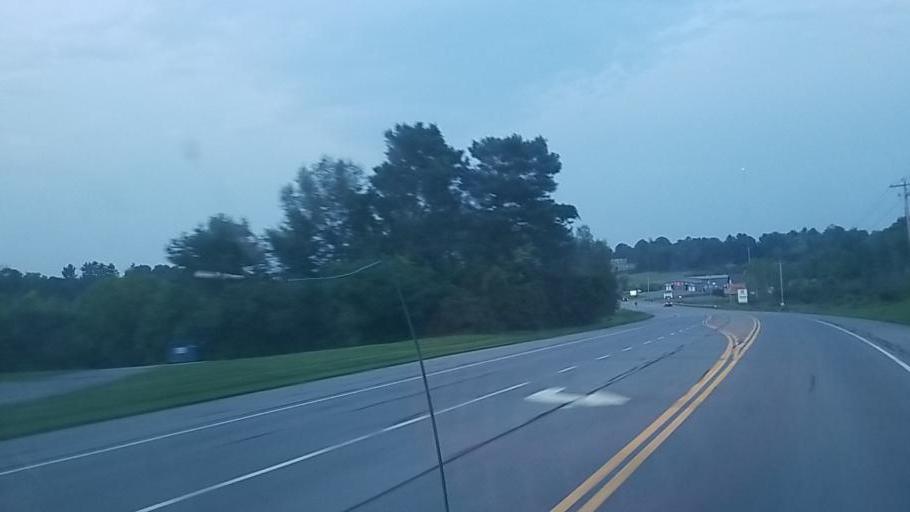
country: US
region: New York
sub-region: Fulton County
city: Johnstown
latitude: 42.9970
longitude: -74.3632
